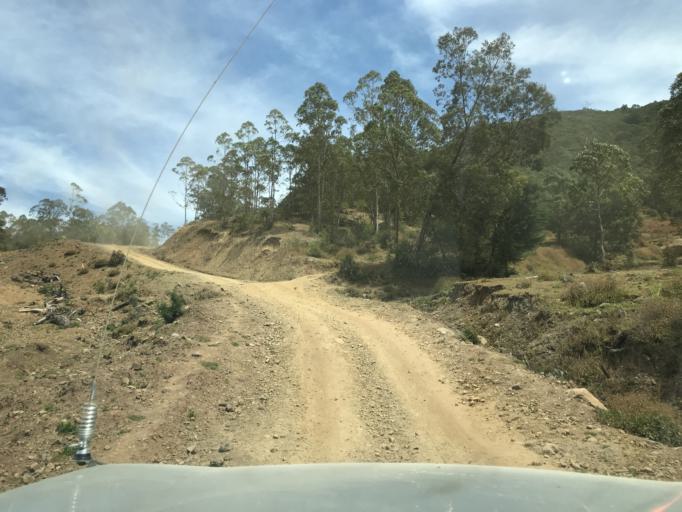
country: TL
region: Ainaro
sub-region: Ainaro
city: Ainaro
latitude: -8.8777
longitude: 125.5321
